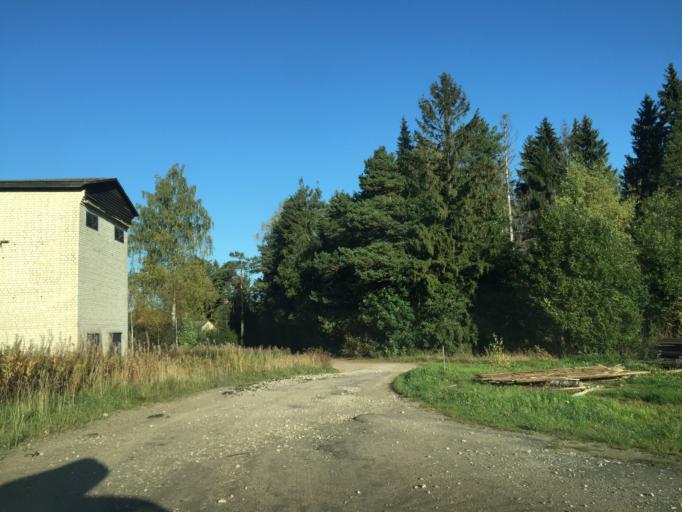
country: LV
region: Vecpiebalga
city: Vecpiebalga
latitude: 57.0673
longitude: 25.7482
